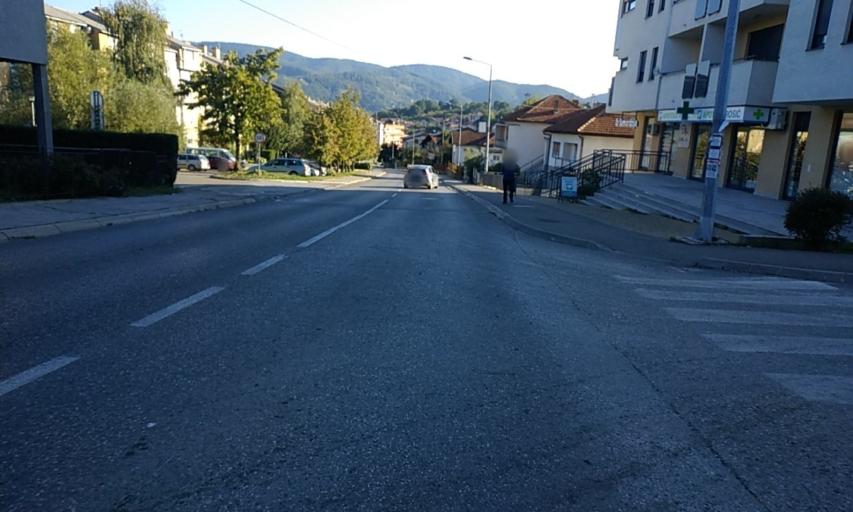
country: BA
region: Republika Srpska
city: Banja Luka
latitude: 44.7768
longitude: 17.1781
